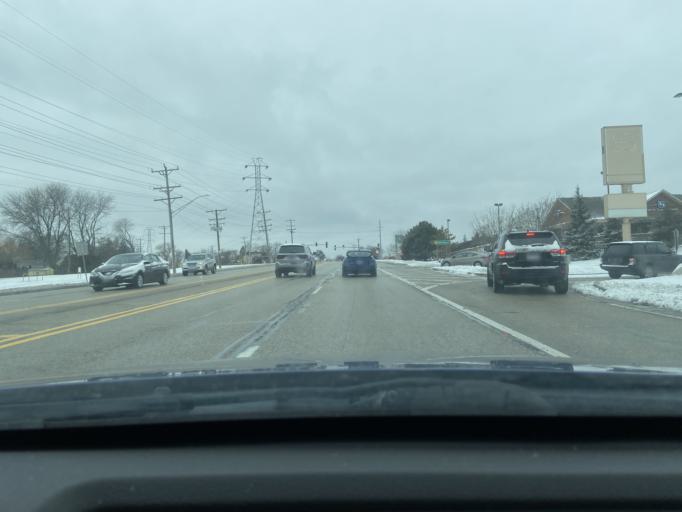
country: US
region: Illinois
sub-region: Lake County
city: Round Lake Beach
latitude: 42.3791
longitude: -88.0708
